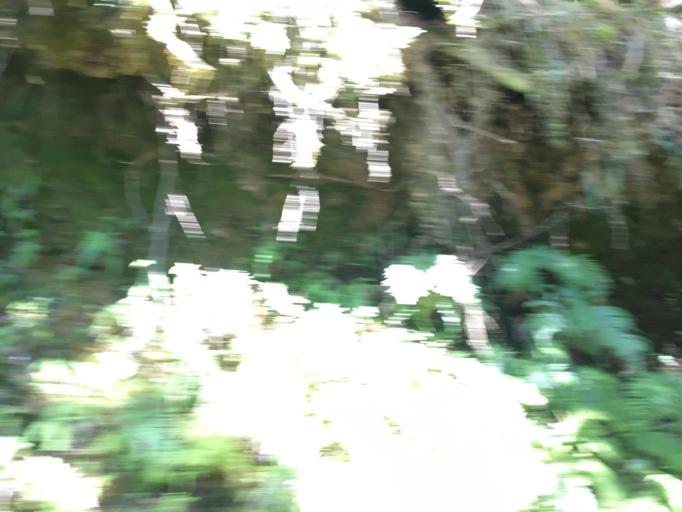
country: TW
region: Taiwan
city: Daxi
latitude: 24.5558
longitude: 121.3973
